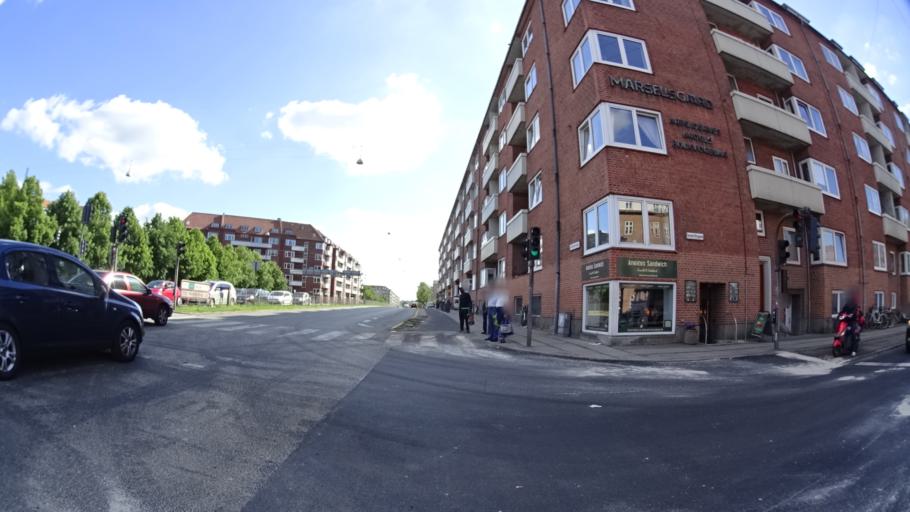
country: DK
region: Central Jutland
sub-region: Arhus Kommune
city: Arhus
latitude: 56.1442
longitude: 10.1895
